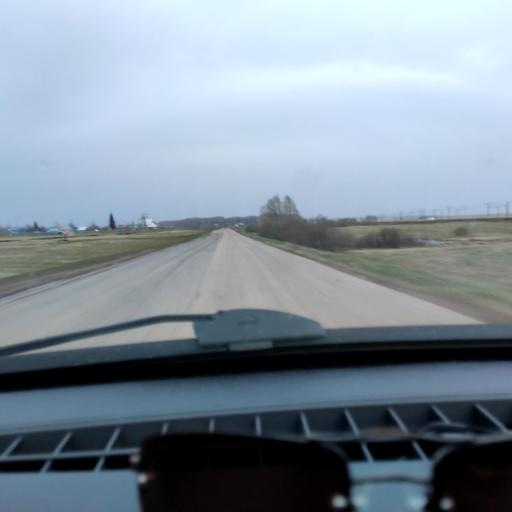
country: RU
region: Bashkortostan
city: Ulukulevo
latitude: 54.4482
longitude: 56.2610
